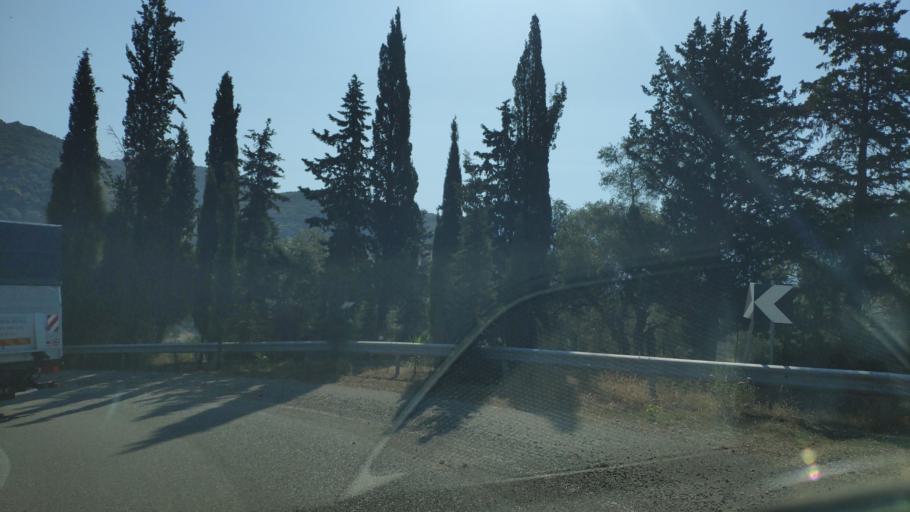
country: GR
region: West Greece
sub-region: Nomos Aitolias kai Akarnanias
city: Stanos
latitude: 38.7728
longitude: 21.1485
